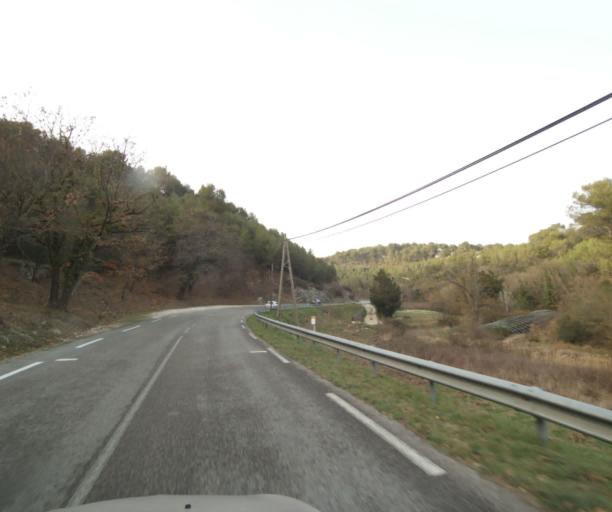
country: FR
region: Provence-Alpes-Cote d'Azur
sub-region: Departement des Bouches-du-Rhone
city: Rognes
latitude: 43.6695
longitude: 5.3530
